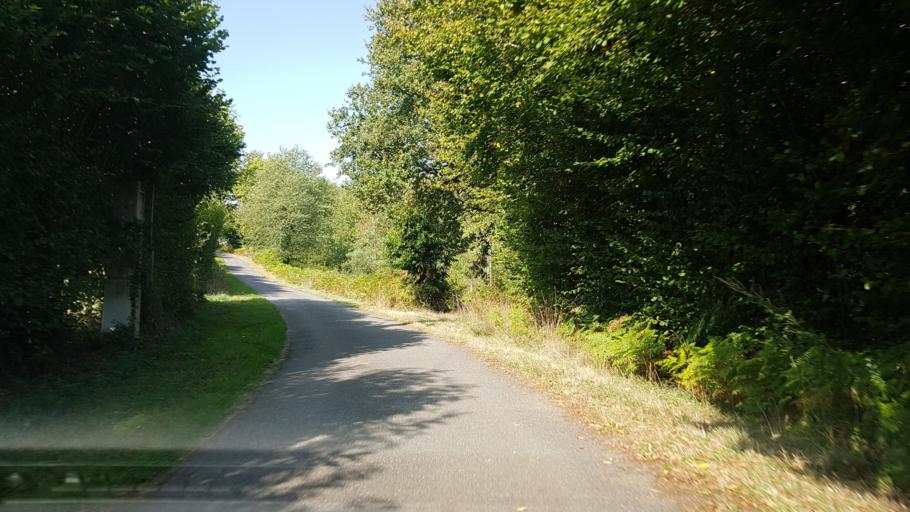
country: FR
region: Poitou-Charentes
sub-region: Departement de la Charente
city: Etagnac
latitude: 45.9234
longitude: 0.7795
